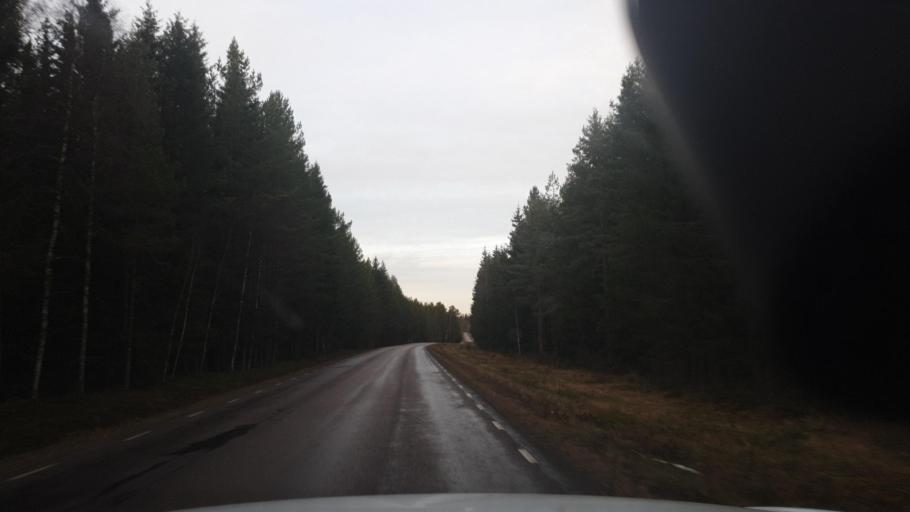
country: SE
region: Vaermland
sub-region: Eda Kommun
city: Amotfors
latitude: 59.7340
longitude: 12.1698
